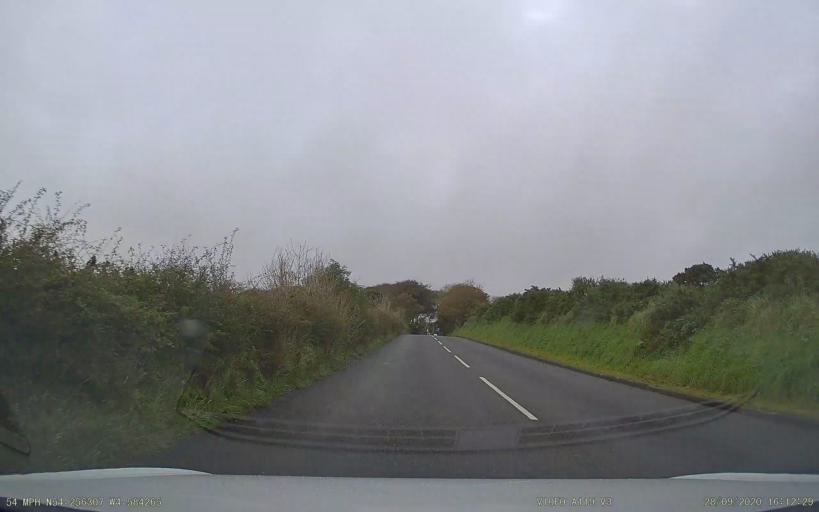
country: IM
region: Douglas
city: Douglas
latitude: 54.2563
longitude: -4.5843
